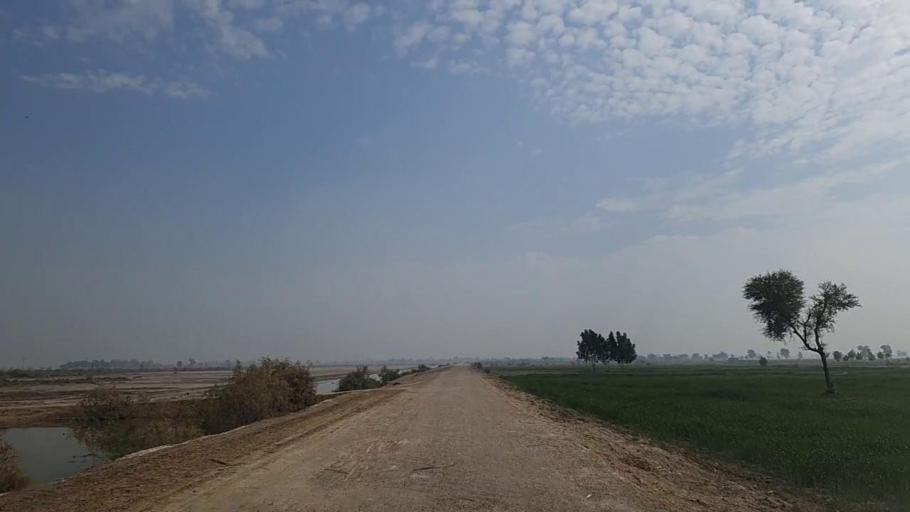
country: PK
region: Sindh
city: Daur
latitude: 26.3842
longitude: 68.3746
